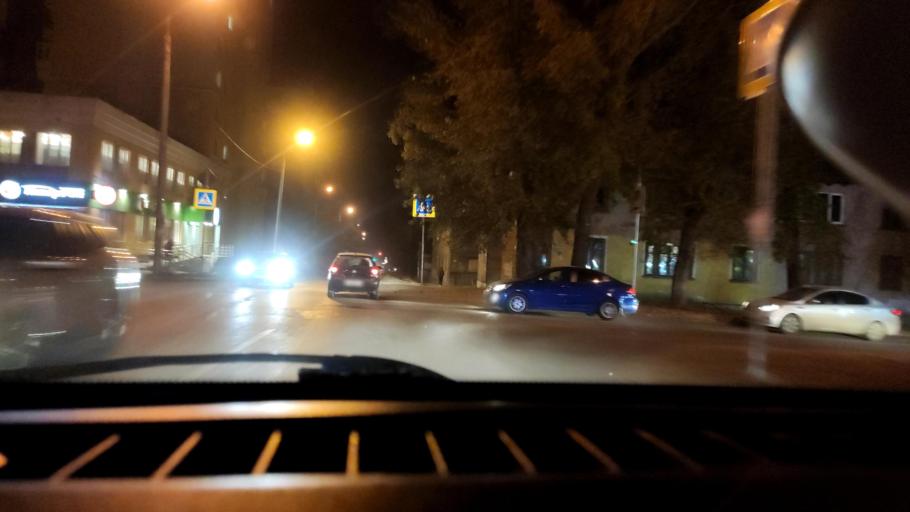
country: RU
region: Samara
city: Samara
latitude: 53.2381
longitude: 50.2604
